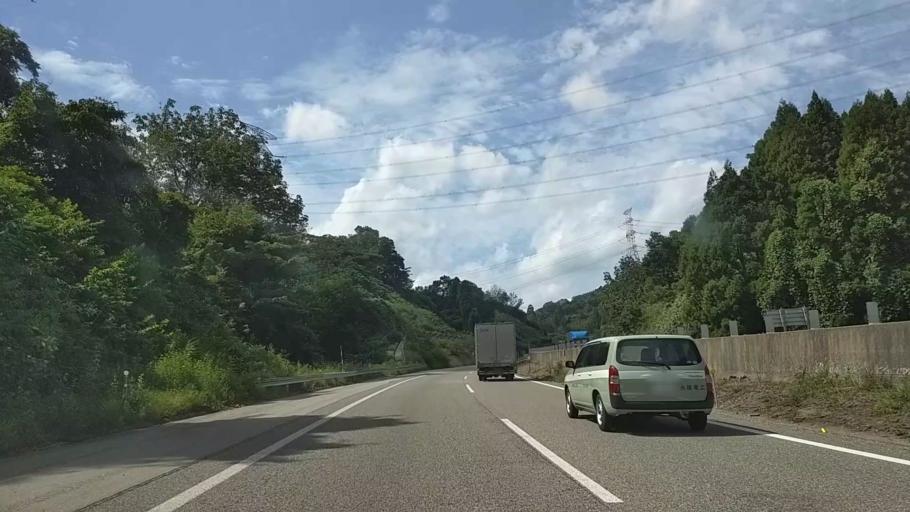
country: JP
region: Toyama
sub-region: Oyabe Shi
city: Oyabe
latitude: 36.6039
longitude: 136.7993
